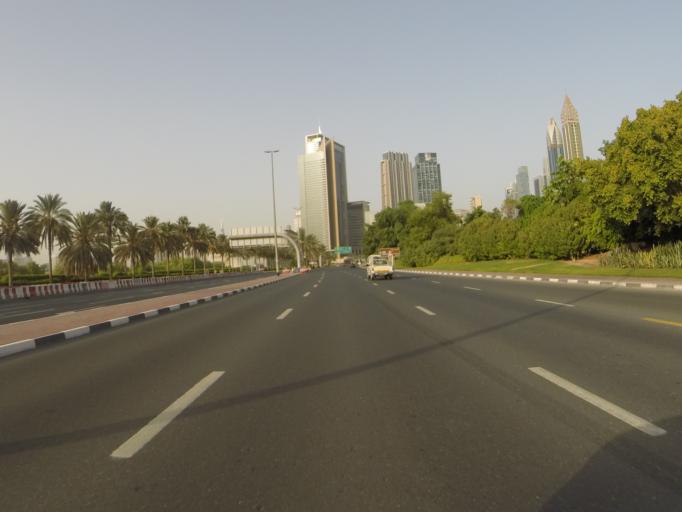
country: AE
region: Ash Shariqah
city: Sharjah
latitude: 25.2171
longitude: 55.2860
